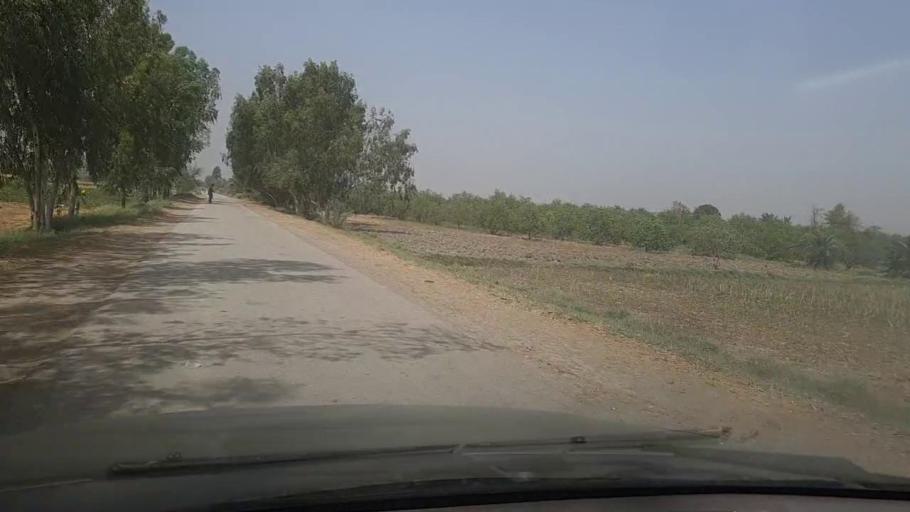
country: PK
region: Sindh
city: Madeji
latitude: 27.7983
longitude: 68.4168
